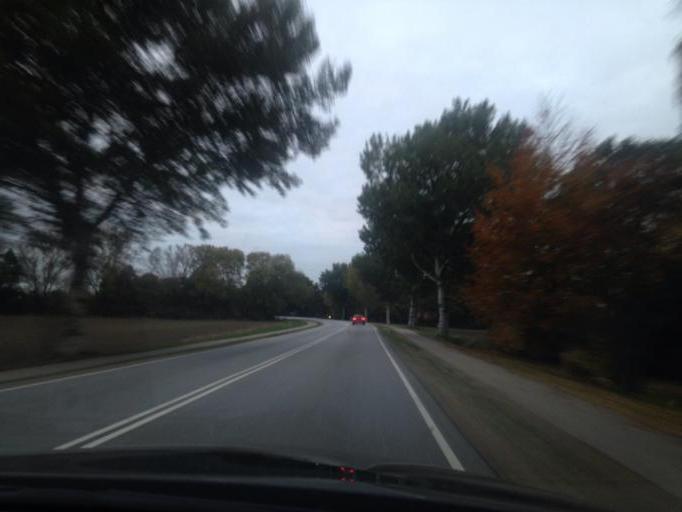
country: DK
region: Zealand
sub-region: Solrod Kommune
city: Havdrup
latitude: 55.5583
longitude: 12.1463
